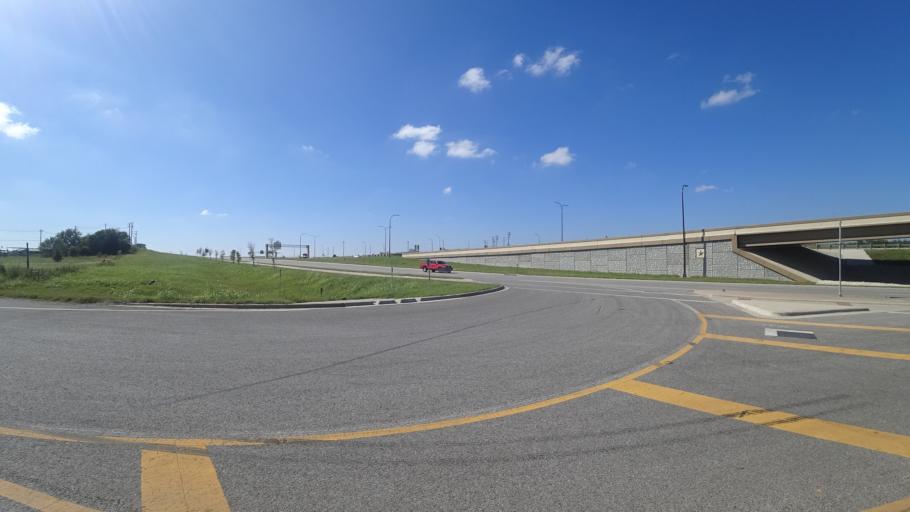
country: US
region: Texas
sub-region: Travis County
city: Manor
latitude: 30.3362
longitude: -97.5999
